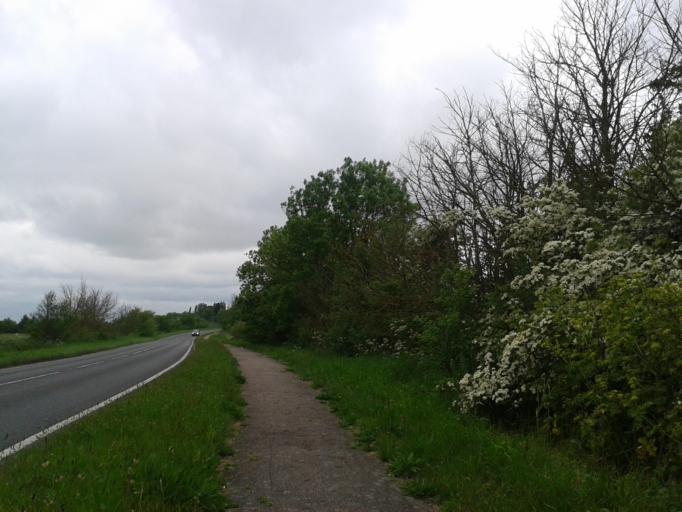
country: GB
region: England
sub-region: Cambridgeshire
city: Great Stukeley
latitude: 52.3474
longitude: -0.2008
